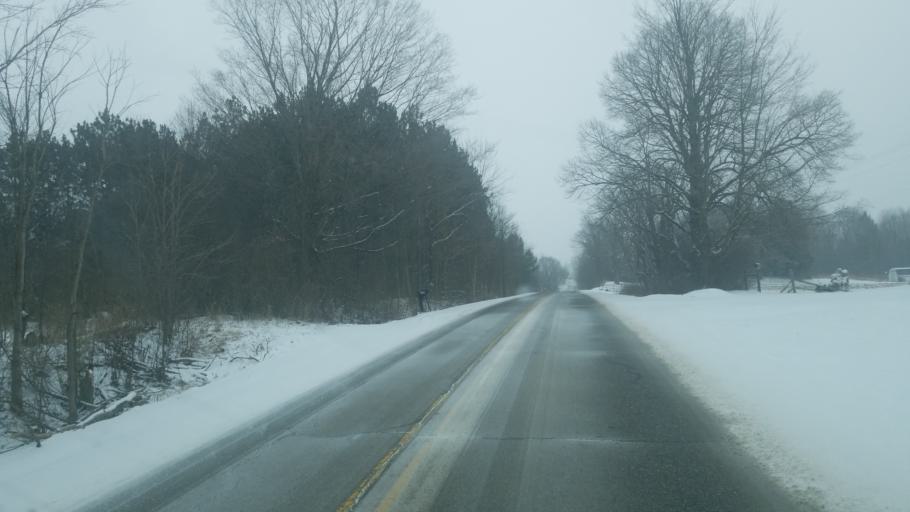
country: US
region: Michigan
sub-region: Osceola County
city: Evart
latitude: 43.8505
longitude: -85.3696
